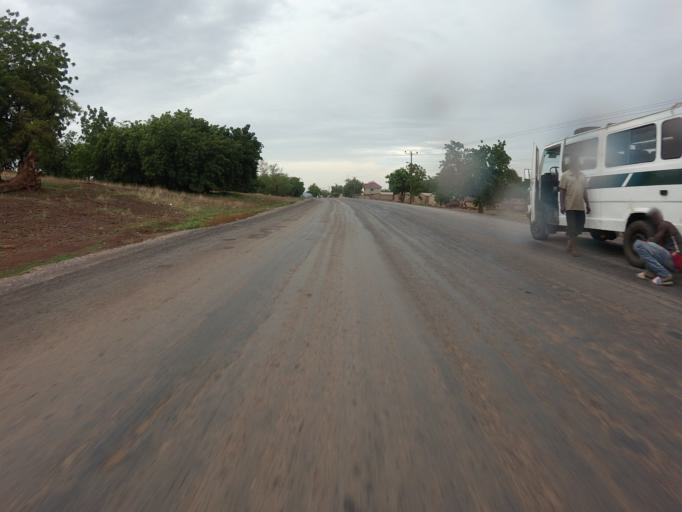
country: GH
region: Upper East
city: Bolgatanga
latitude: 10.8558
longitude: -0.6686
